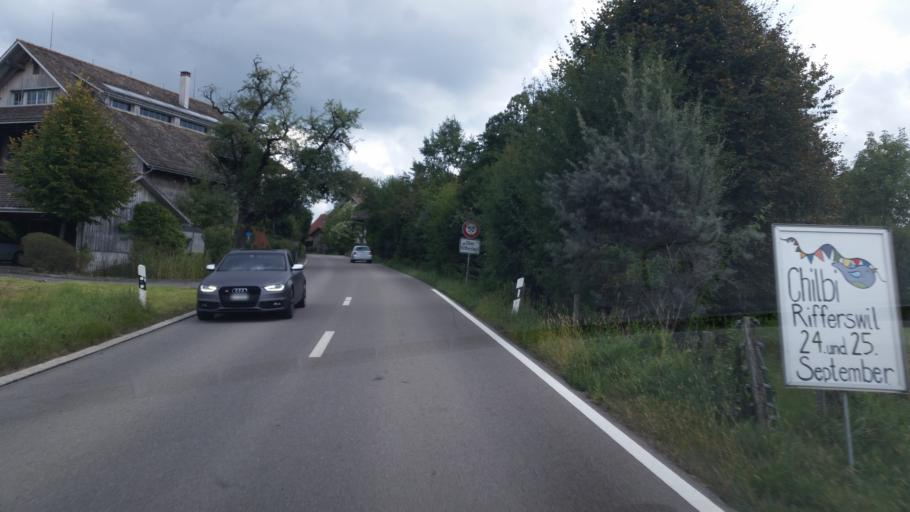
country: CH
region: Zurich
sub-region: Bezirk Affoltern
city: Mettmenstetten
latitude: 47.2426
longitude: 8.4922
